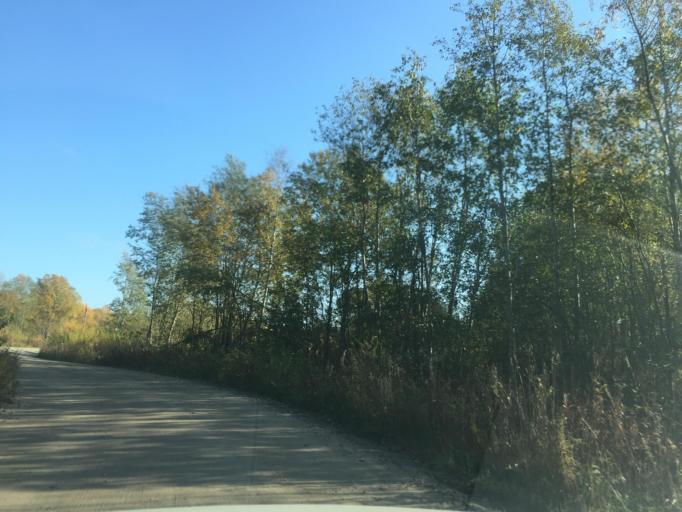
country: RU
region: Republic of Karelia
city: Lakhdenpokh'ya
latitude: 61.2938
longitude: 30.0678
